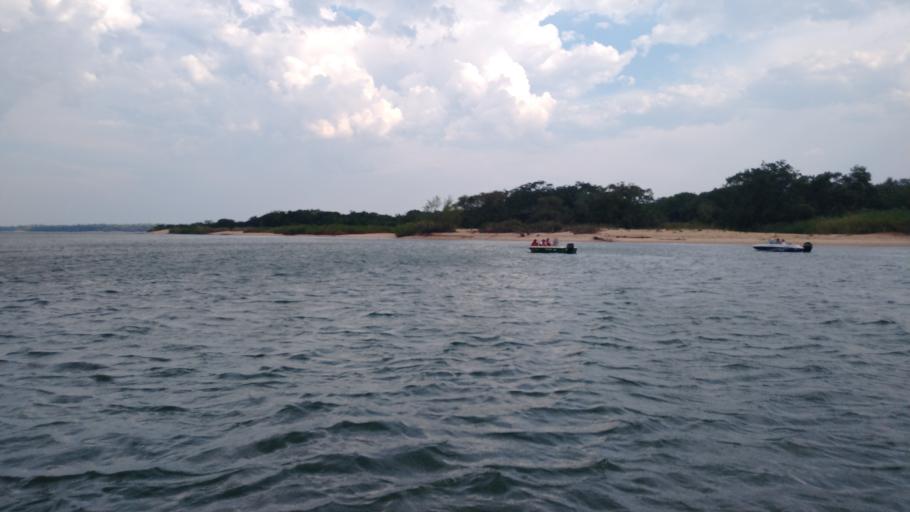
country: PY
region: Neembucu
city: Cerrito
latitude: -27.3476
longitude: -57.6822
